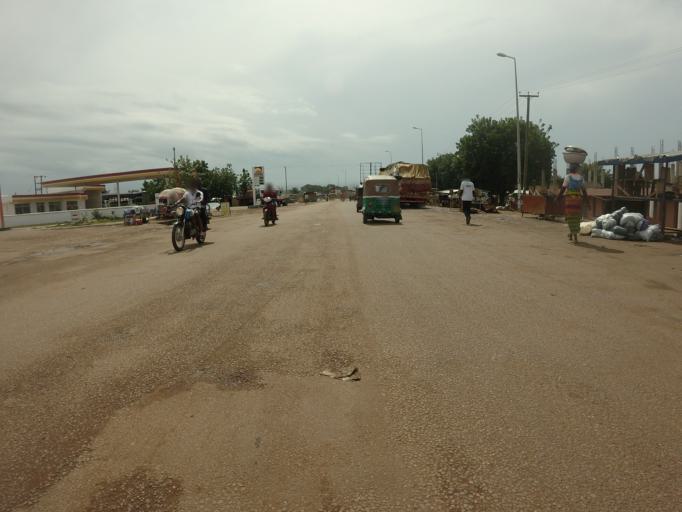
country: GH
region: Upper East
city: Bolgatanga
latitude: 10.7843
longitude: -0.8470
